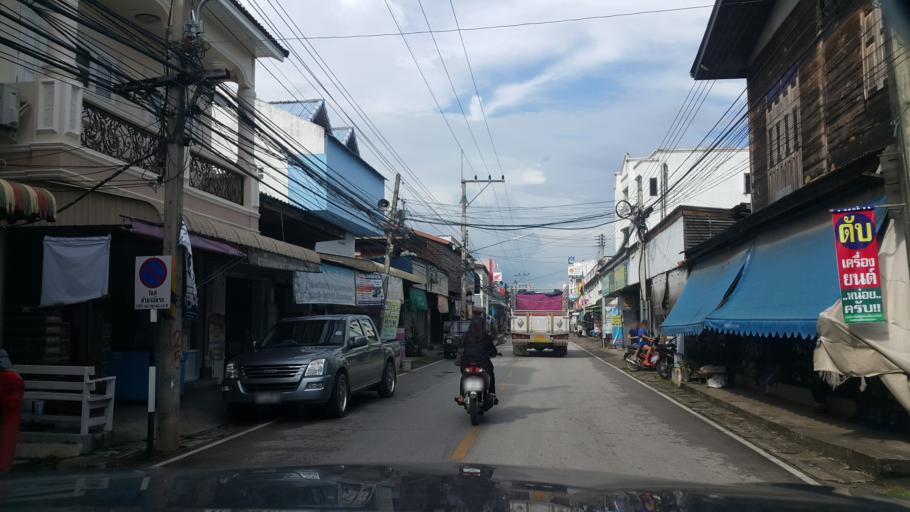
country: TH
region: Lampang
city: Thoen
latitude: 17.6058
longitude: 99.2101
